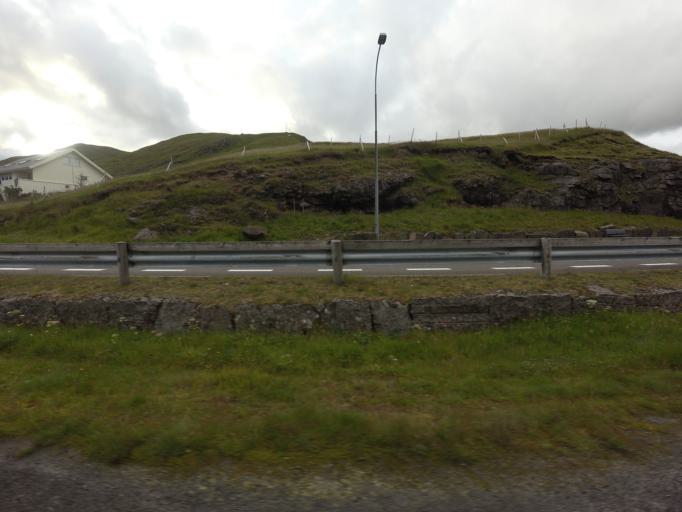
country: FO
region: Streymoy
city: Kollafjordhur
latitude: 62.1203
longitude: -6.8746
